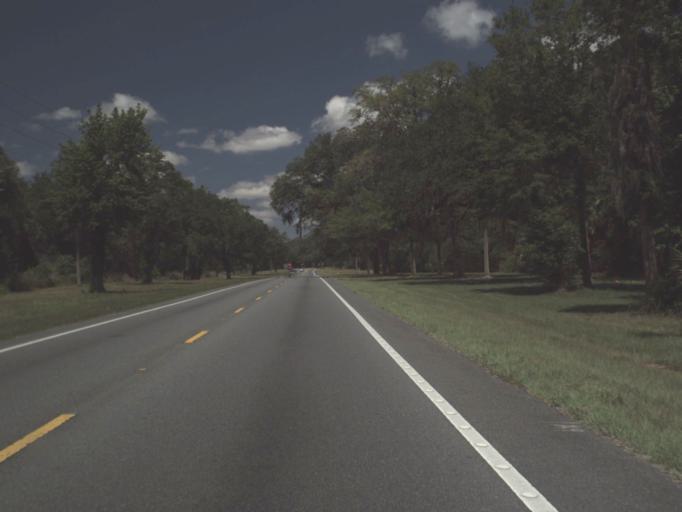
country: US
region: Florida
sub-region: Marion County
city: Silver Springs Shores
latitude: 29.2186
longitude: -82.0221
